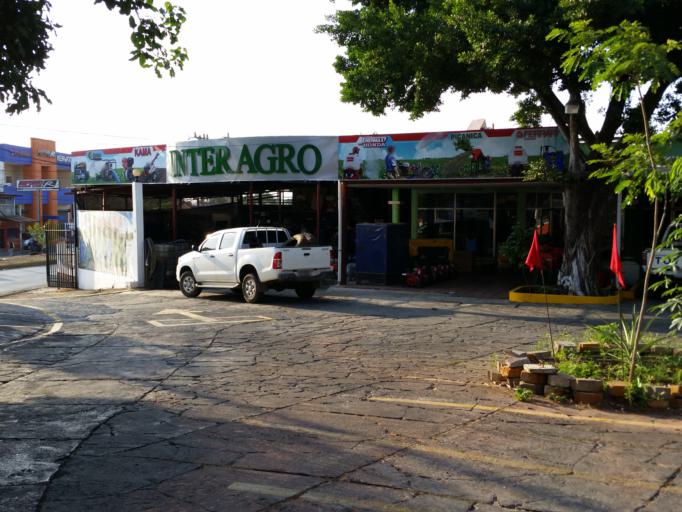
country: NI
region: Managua
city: Managua
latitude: 12.1303
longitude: -86.2562
